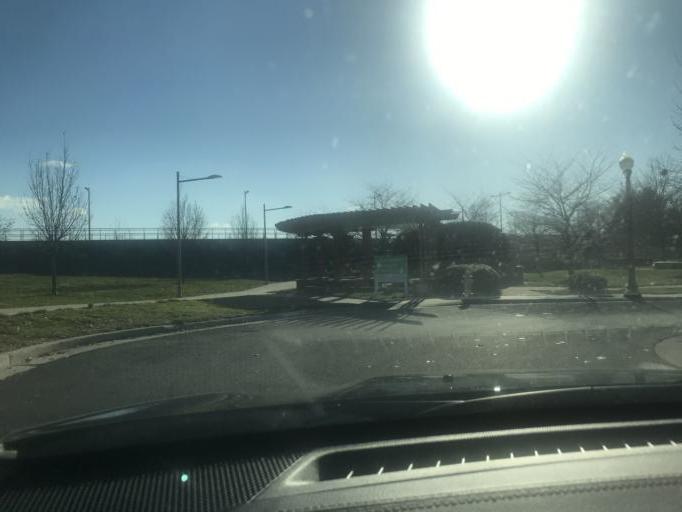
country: US
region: Washington, D.C.
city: Washington, D.C.
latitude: 38.8645
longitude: -77.0481
